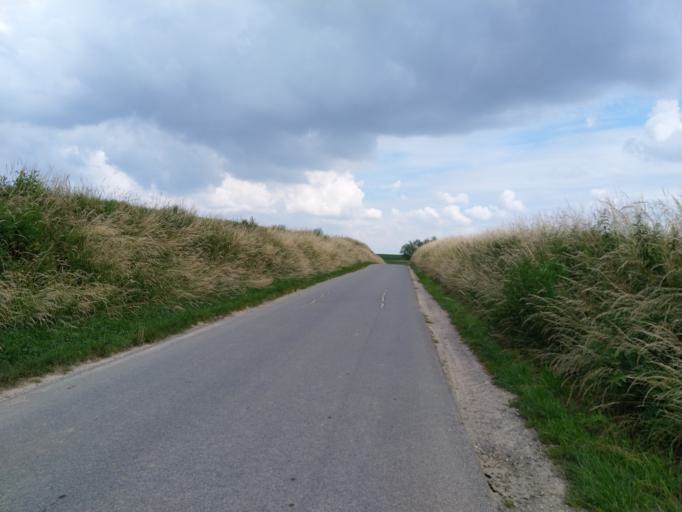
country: FR
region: Nord-Pas-de-Calais
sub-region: Departement du Nord
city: Boussois
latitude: 50.3453
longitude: 4.0211
